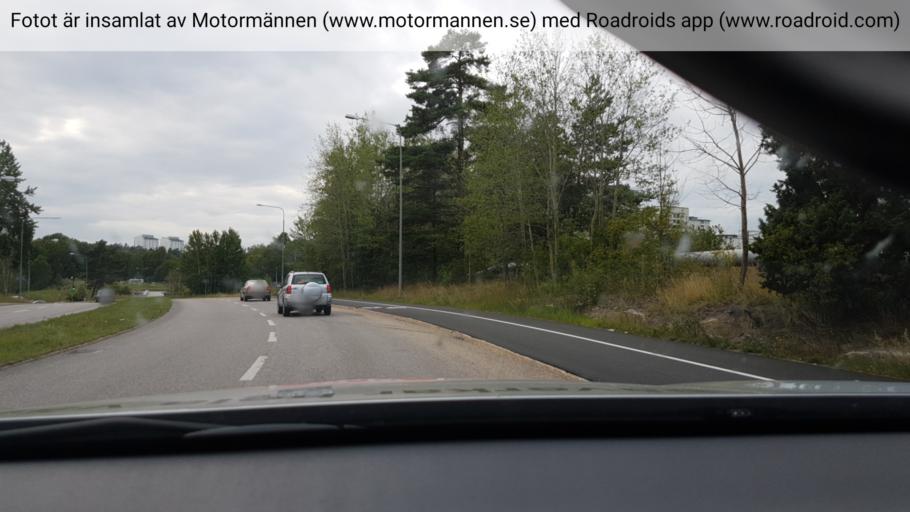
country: SE
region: Stockholm
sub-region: Stockholms Kommun
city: Arsta
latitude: 59.2596
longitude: 18.0443
